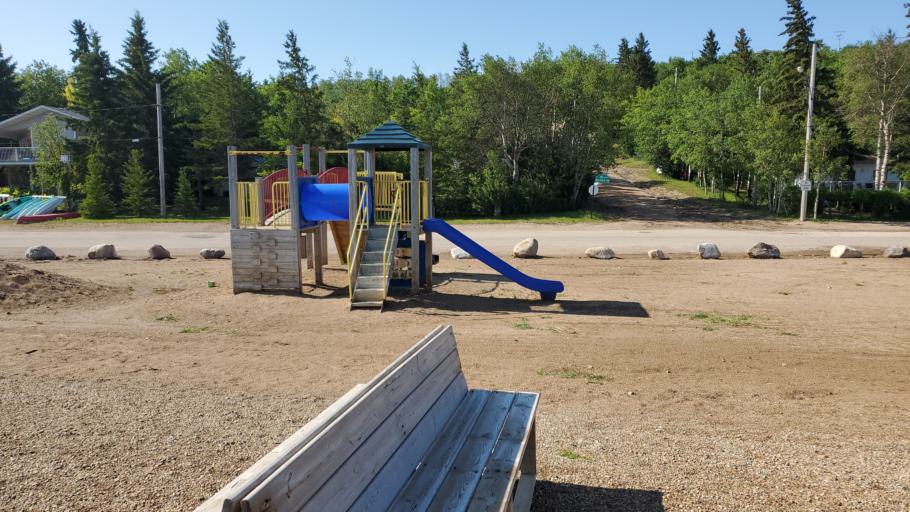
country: CA
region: Saskatchewan
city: Watrous
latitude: 51.7219
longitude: -105.4504
